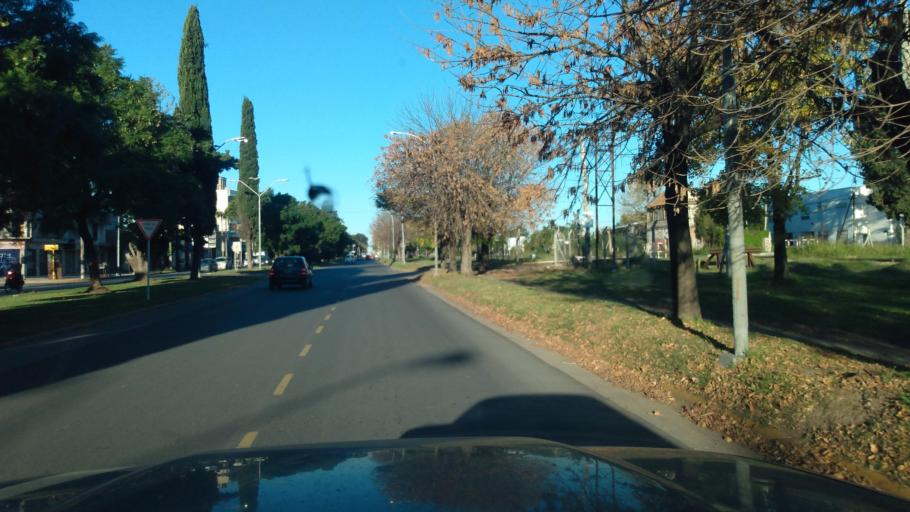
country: AR
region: Buenos Aires
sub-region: Partido de General Rodriguez
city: General Rodriguez
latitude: -34.6105
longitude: -58.9449
